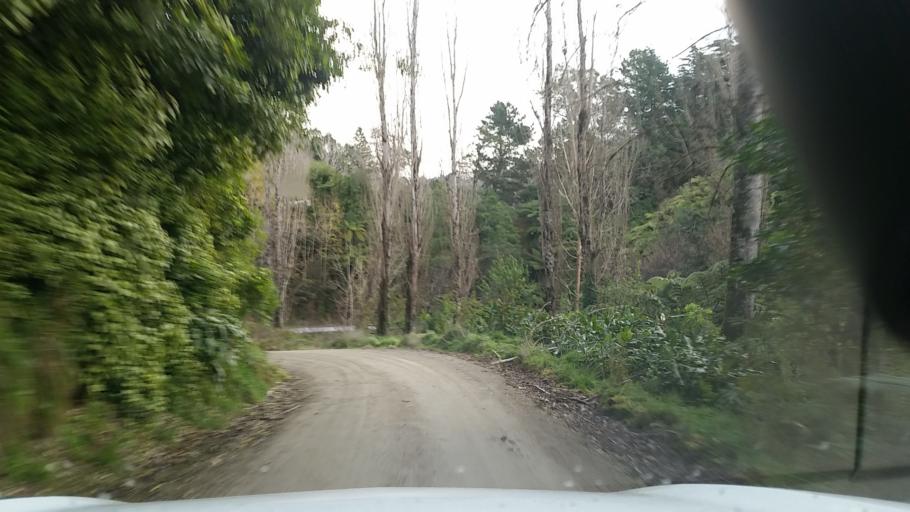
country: NZ
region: Taranaki
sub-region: South Taranaki District
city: Patea
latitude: -39.5665
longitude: 174.8100
